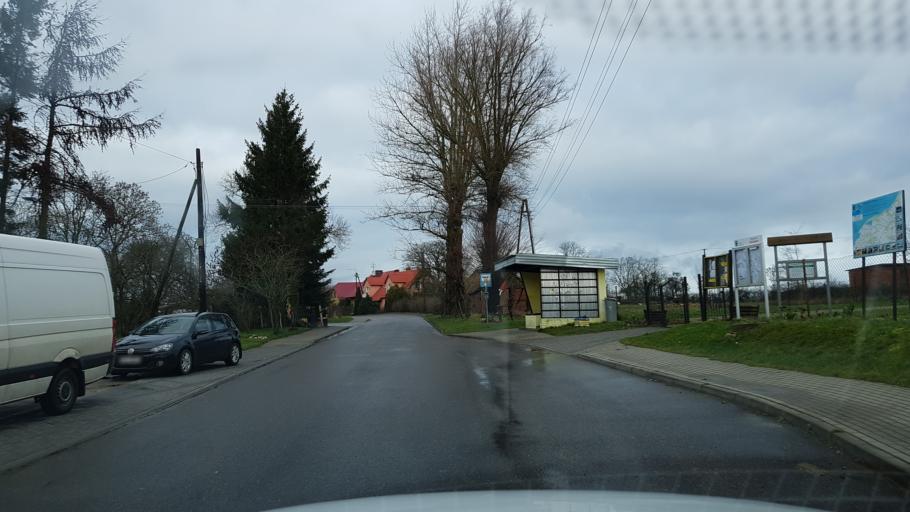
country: PL
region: West Pomeranian Voivodeship
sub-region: Powiat slawienski
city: Slawno
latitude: 54.5138
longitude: 16.6548
